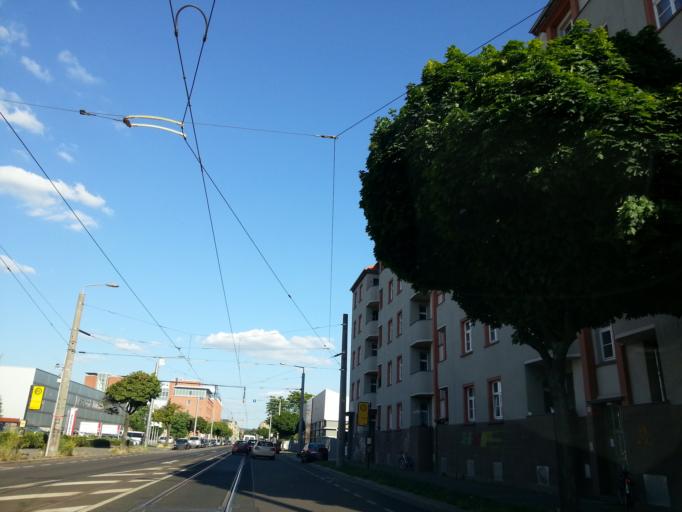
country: DE
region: Saxony
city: Dresden
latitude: 51.0753
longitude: 13.7344
